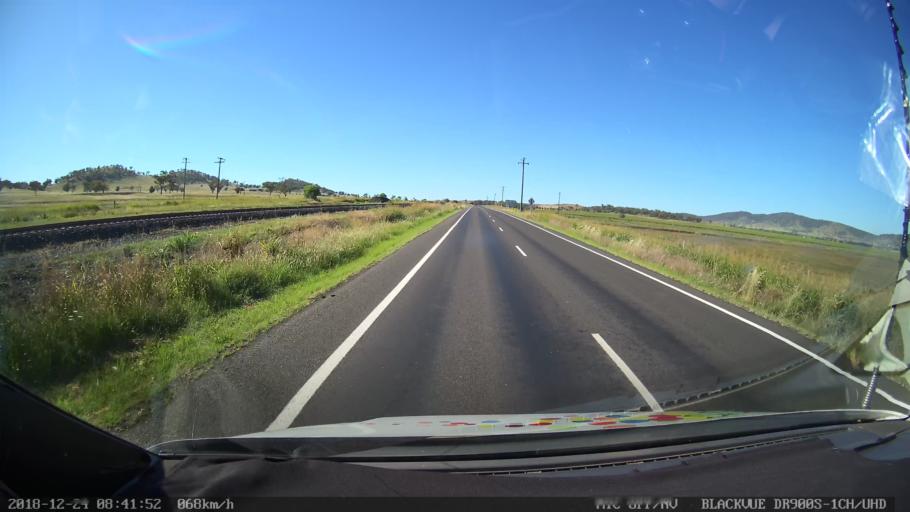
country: AU
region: New South Wales
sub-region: Liverpool Plains
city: Quirindi
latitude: -31.3672
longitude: 150.6440
